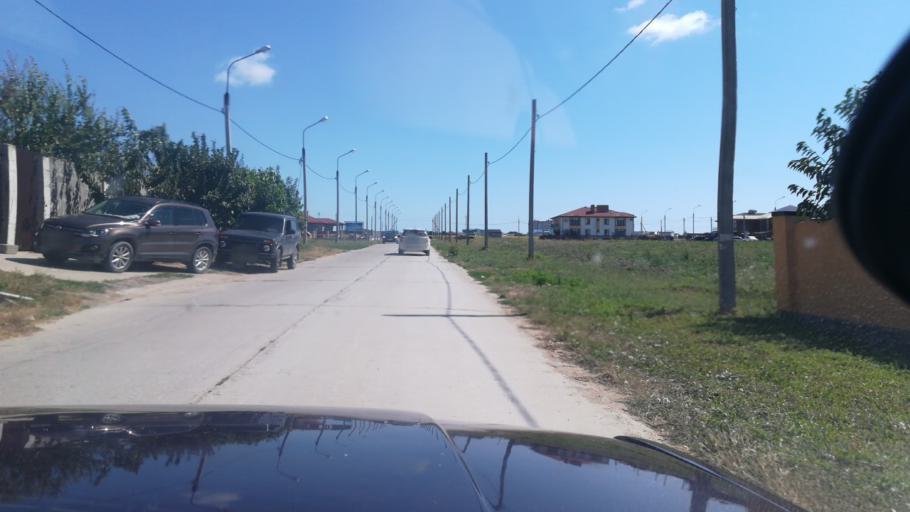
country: RU
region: Krasnodarskiy
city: Vityazevo
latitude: 44.9908
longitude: 37.2755
